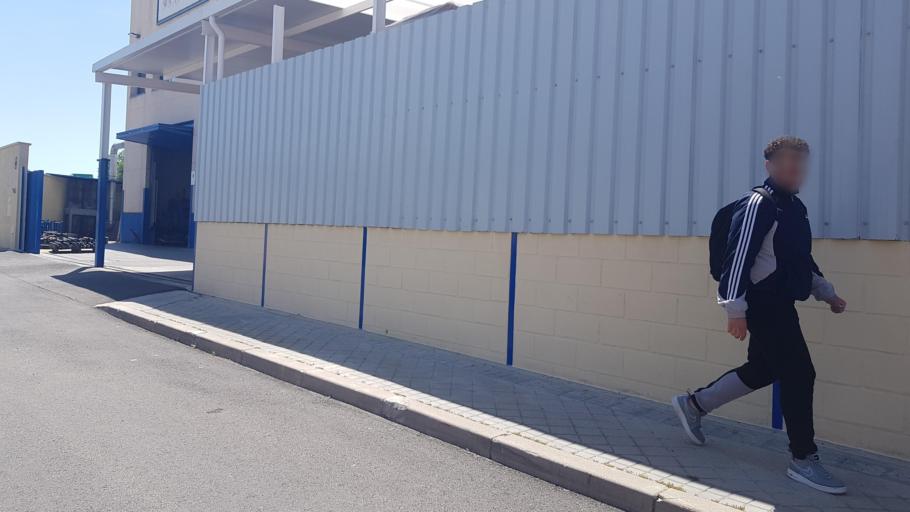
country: ES
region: Madrid
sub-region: Provincia de Madrid
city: Coslada
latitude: 40.4414
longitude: -3.5664
